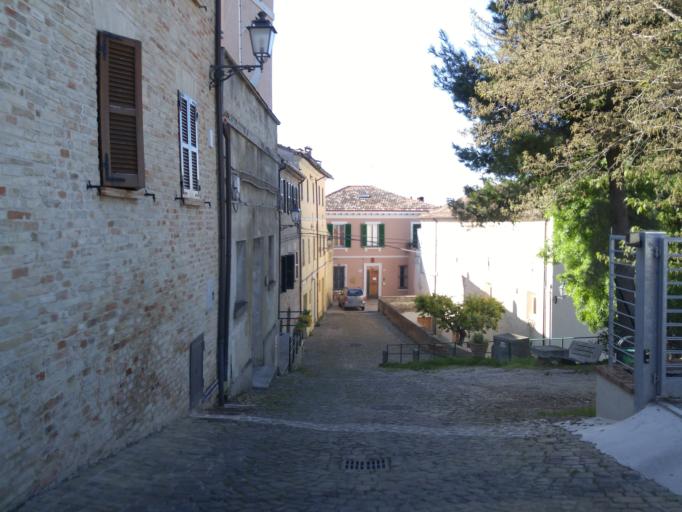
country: IT
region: The Marches
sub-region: Provincia di Pesaro e Urbino
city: Monteciccardo
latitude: 43.8301
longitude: 12.8157
